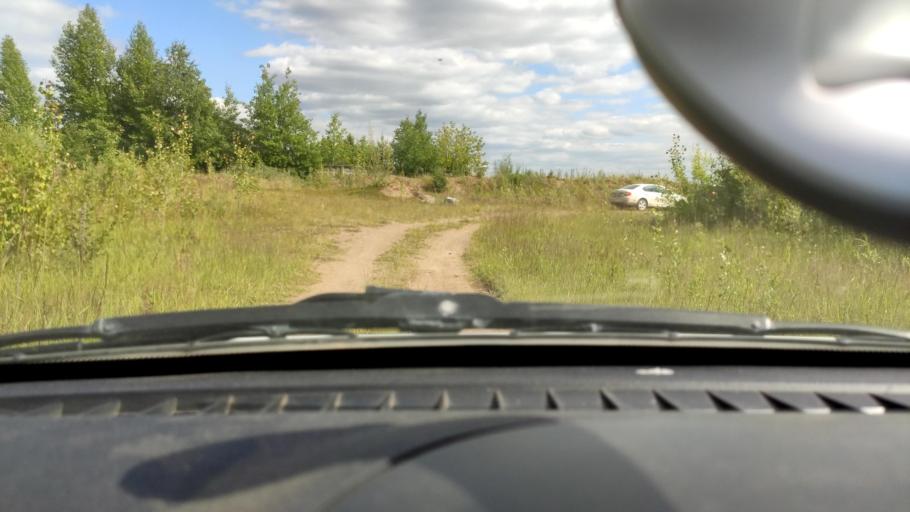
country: RU
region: Perm
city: Kondratovo
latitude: 58.0225
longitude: 56.0728
